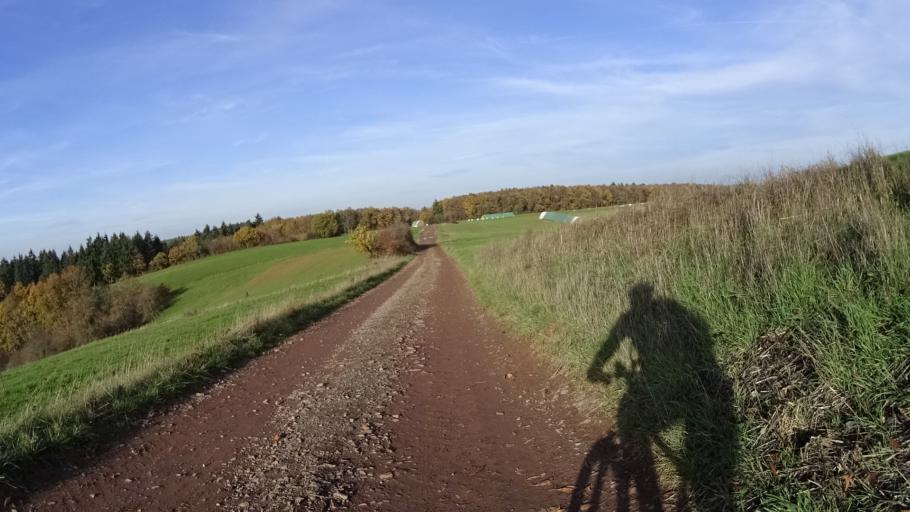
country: DE
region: Rheinland-Pfalz
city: Sienhachenbach
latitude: 49.6976
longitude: 7.4902
